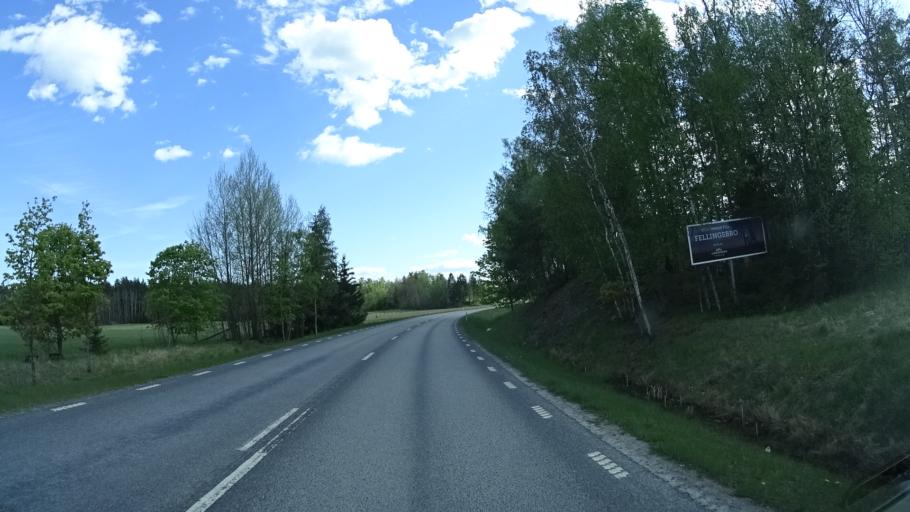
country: SE
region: OErebro
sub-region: Lindesbergs Kommun
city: Fellingsbro
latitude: 59.4434
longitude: 15.5957
